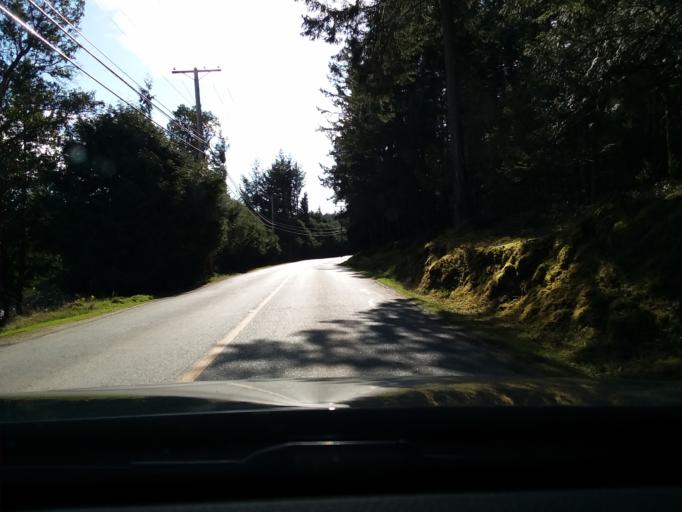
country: CA
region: British Columbia
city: North Saanich
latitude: 48.8833
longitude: -123.3288
